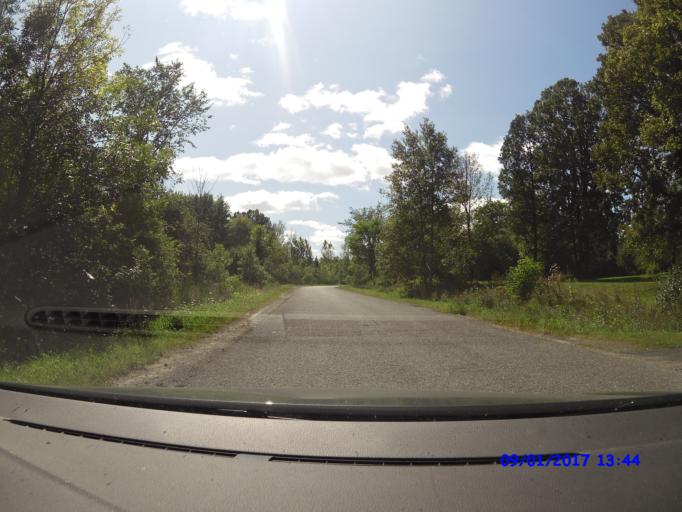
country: CA
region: Ontario
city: Bells Corners
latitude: 45.3640
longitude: -75.9703
